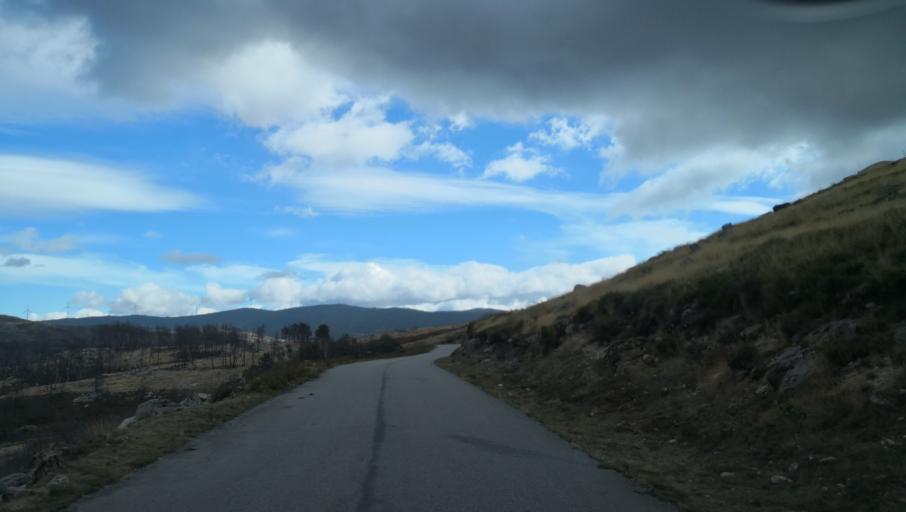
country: PT
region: Vila Real
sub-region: Vila Real
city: Vila Real
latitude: 41.3757
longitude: -7.8237
